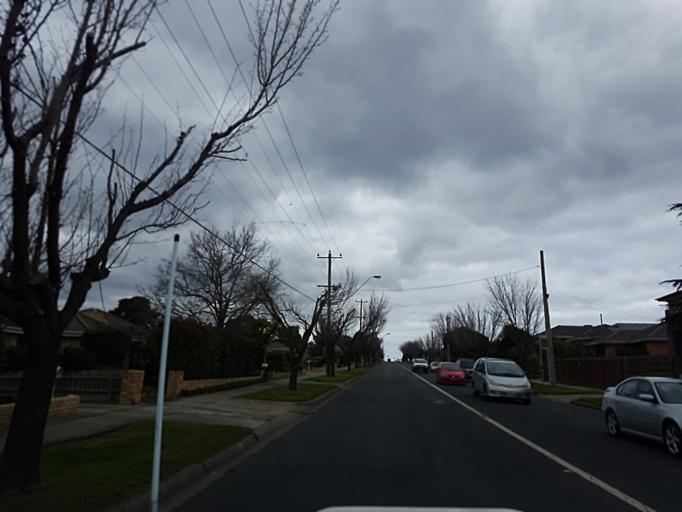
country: AU
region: Victoria
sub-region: Whitehorse
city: Blackburn North
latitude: -37.8050
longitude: 145.1413
